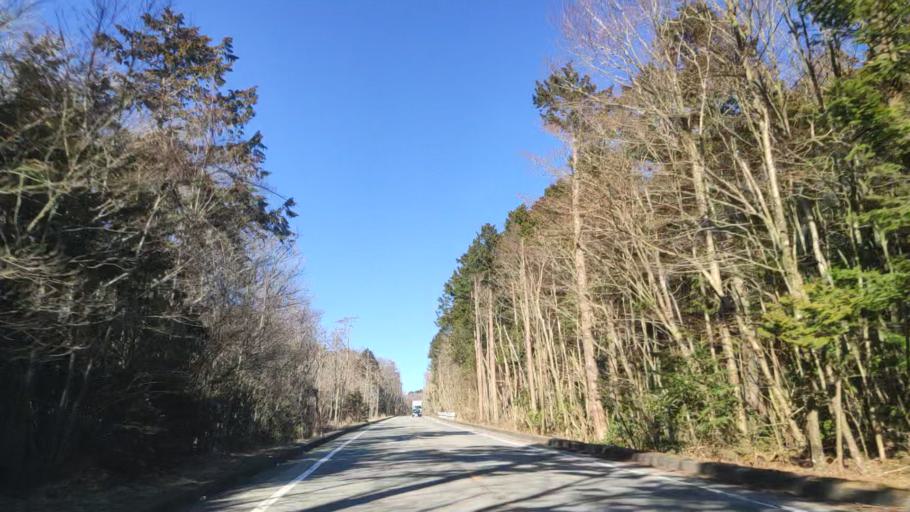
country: JP
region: Yamanashi
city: Fujikawaguchiko
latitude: 35.4330
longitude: 138.6362
